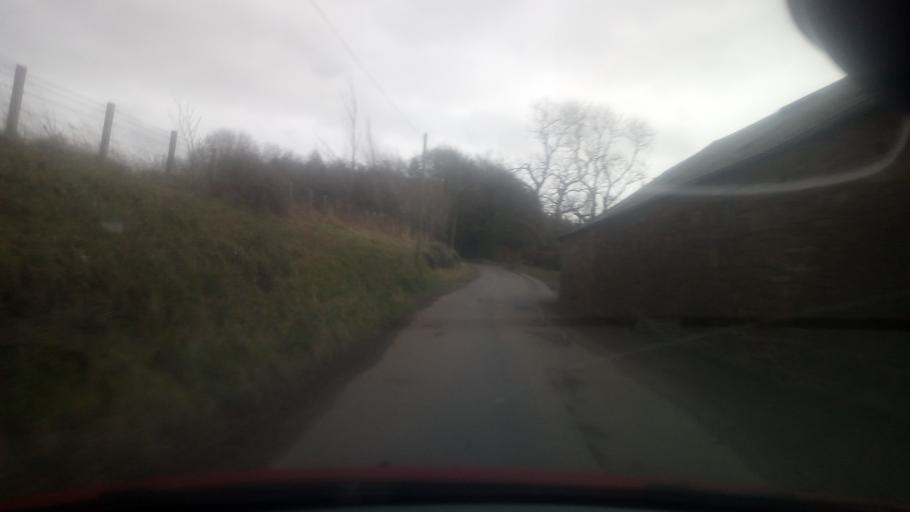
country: GB
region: Scotland
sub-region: The Scottish Borders
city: Jedburgh
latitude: 55.4713
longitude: -2.5379
